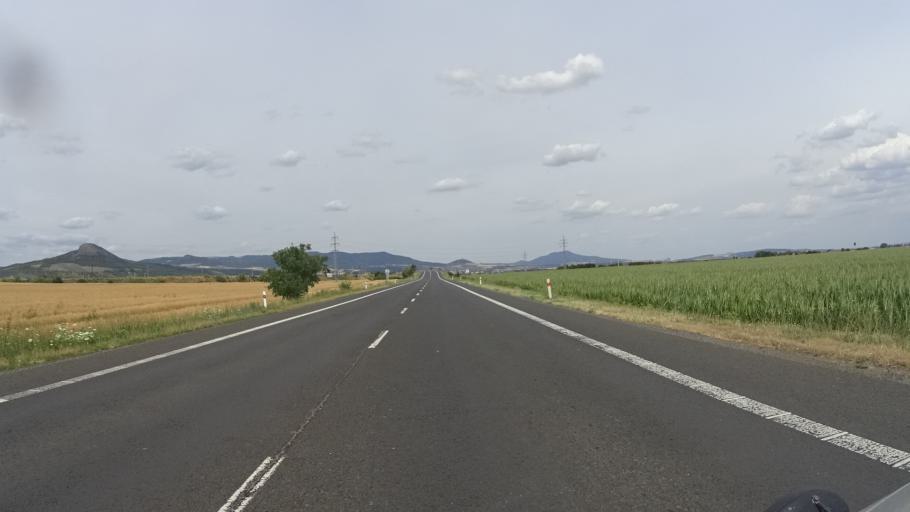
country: CZ
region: Ustecky
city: Lovosice
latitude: 50.4985
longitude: 14.0929
